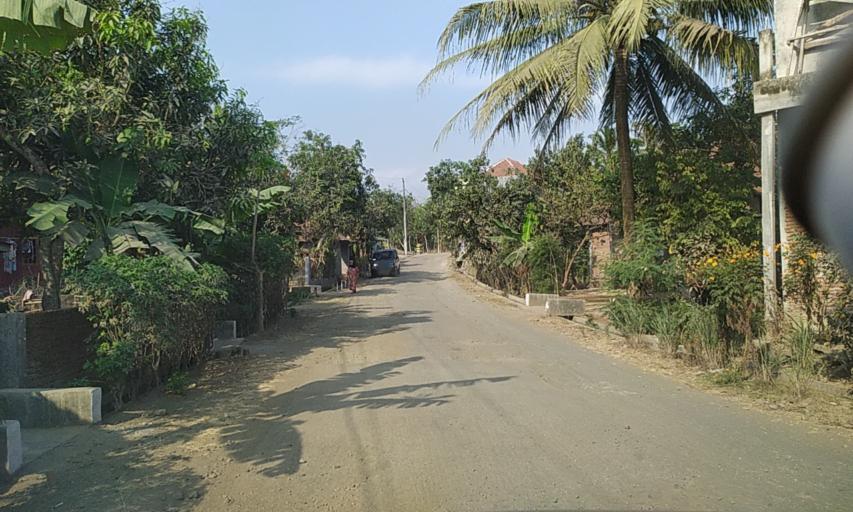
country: ID
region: Central Java
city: Karanggintung
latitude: -7.4837
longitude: 108.9113
